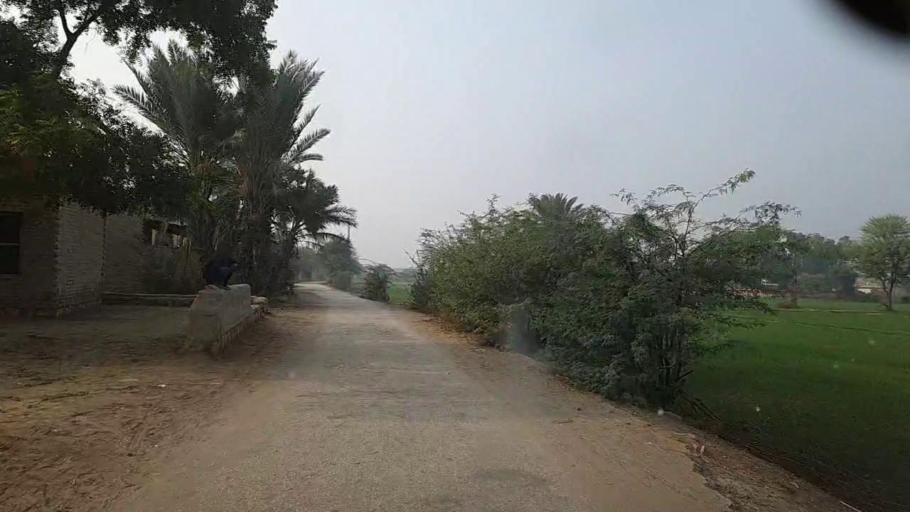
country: PK
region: Sindh
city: Bozdar
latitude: 27.1699
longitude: 68.6574
